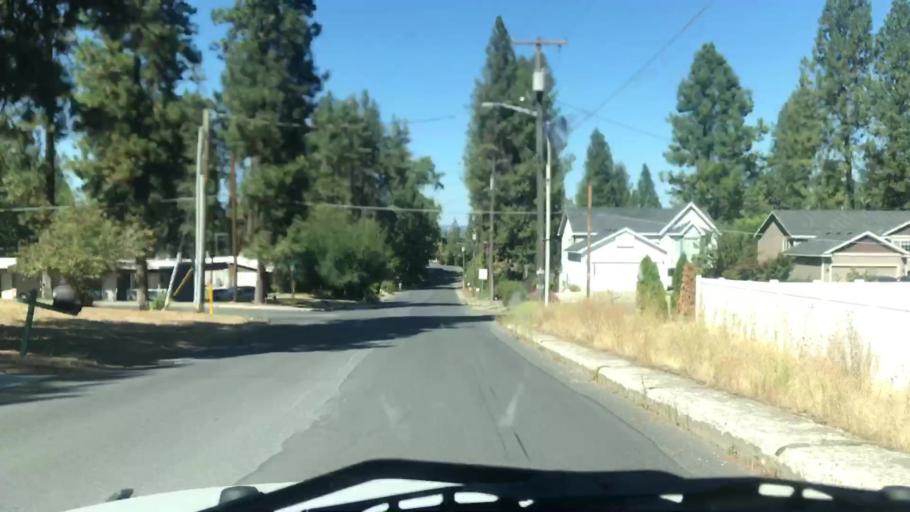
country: US
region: Washington
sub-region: Spokane County
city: Spokane
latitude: 47.6425
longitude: -117.4515
